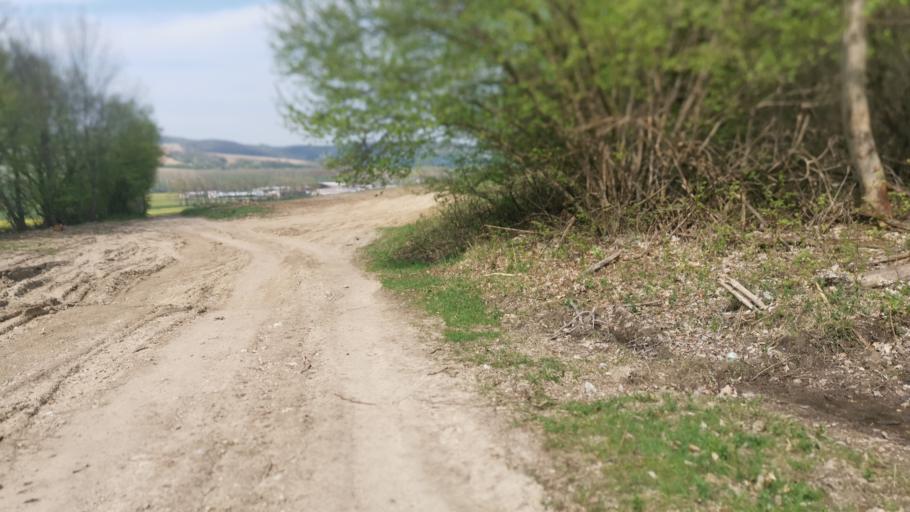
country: SK
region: Trnavsky
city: Smolenice
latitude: 48.5318
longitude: 17.3816
